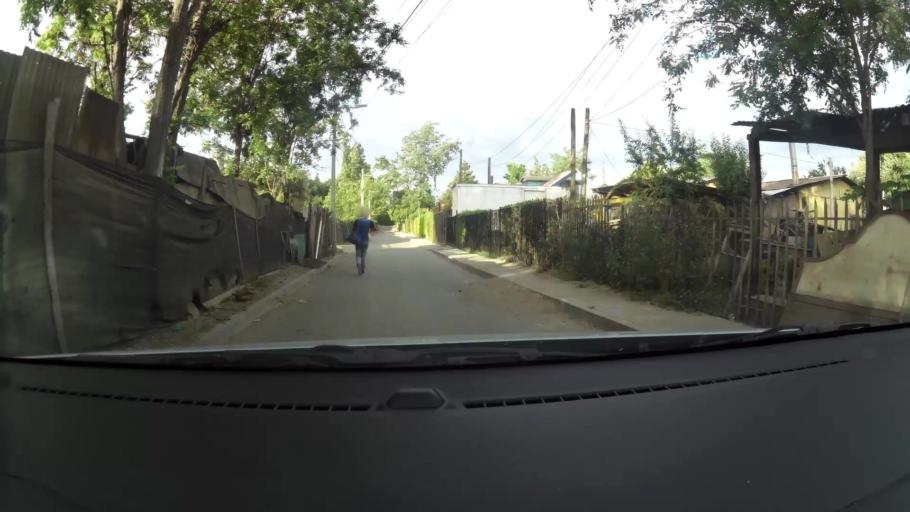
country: CL
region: Santiago Metropolitan
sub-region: Provincia de Maipo
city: San Bernardo
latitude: -33.6454
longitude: -70.6660
